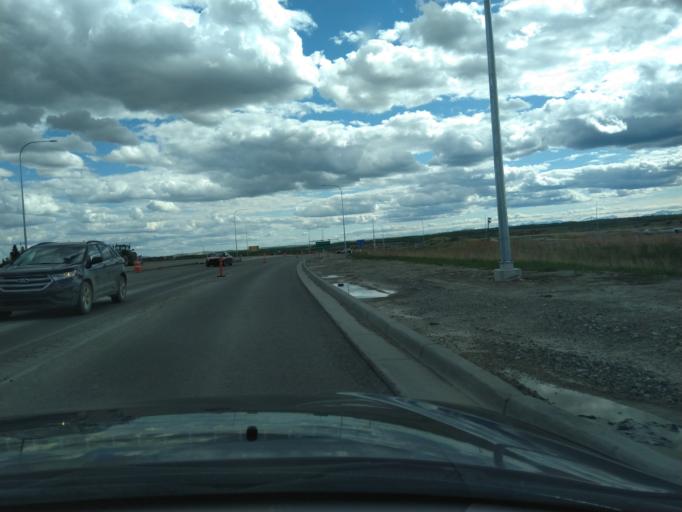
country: CA
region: Alberta
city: Calgary
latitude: 51.0058
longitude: -114.1420
